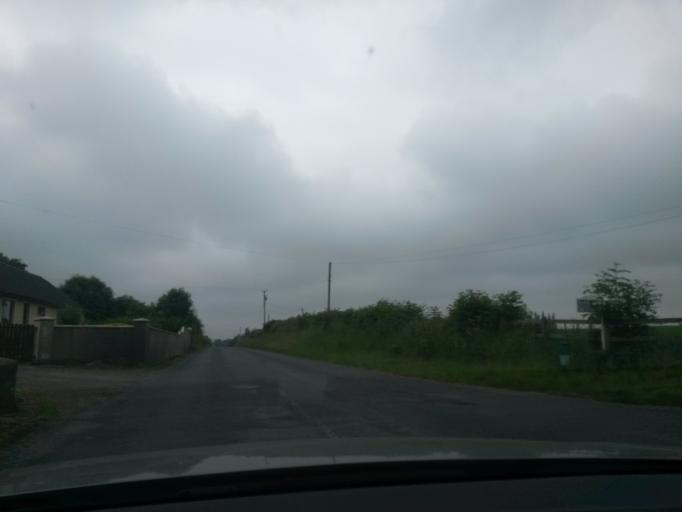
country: IE
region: Munster
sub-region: Ciarrai
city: Tralee
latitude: 52.3897
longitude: -9.6872
